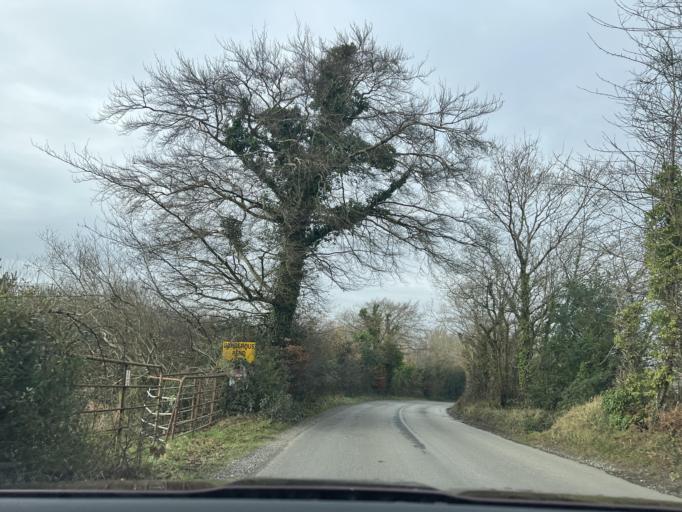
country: IE
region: Leinster
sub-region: Loch Garman
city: Castlebridge
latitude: 52.3809
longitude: -6.5531
